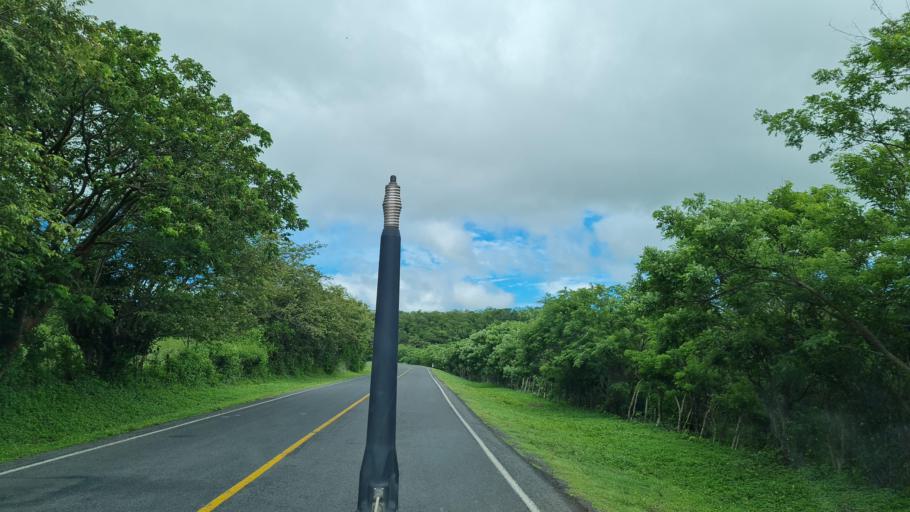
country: NI
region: Matagalpa
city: Terrabona
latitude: 12.5826
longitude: -85.9774
